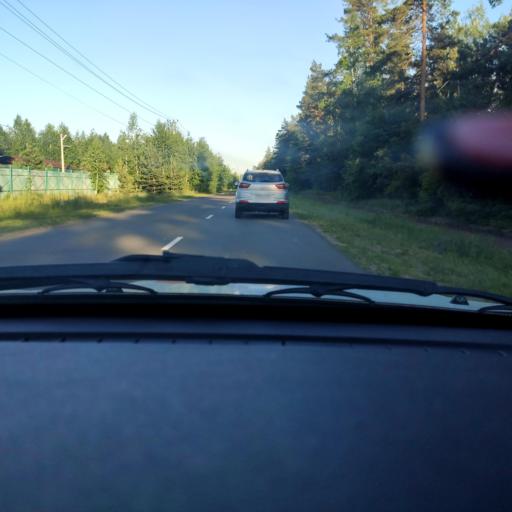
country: RU
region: Voronezj
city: Ramon'
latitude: 51.8900
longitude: 39.2473
